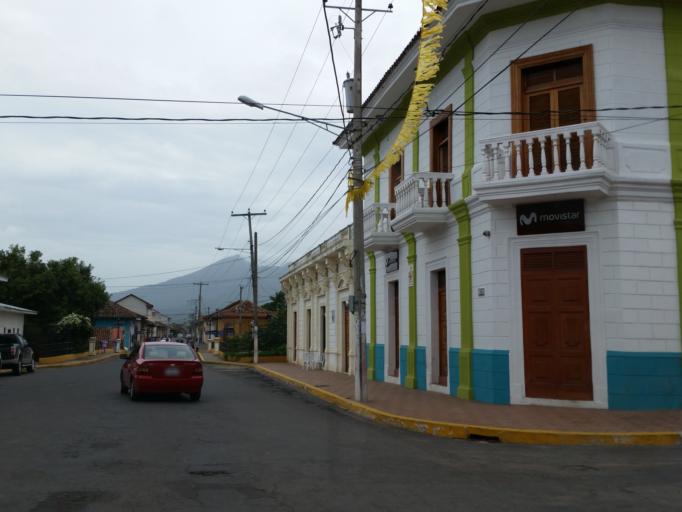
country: NI
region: Granada
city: Granada
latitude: 11.9346
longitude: -85.9553
